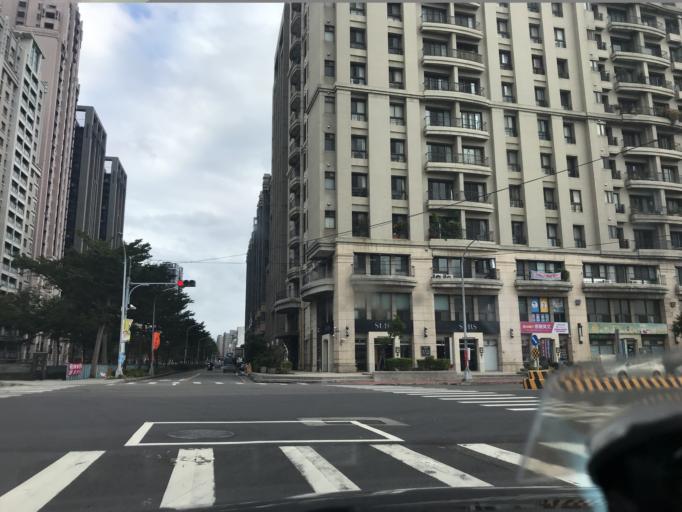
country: TW
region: Taiwan
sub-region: Hsinchu
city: Zhubei
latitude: 24.8267
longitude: 121.0245
